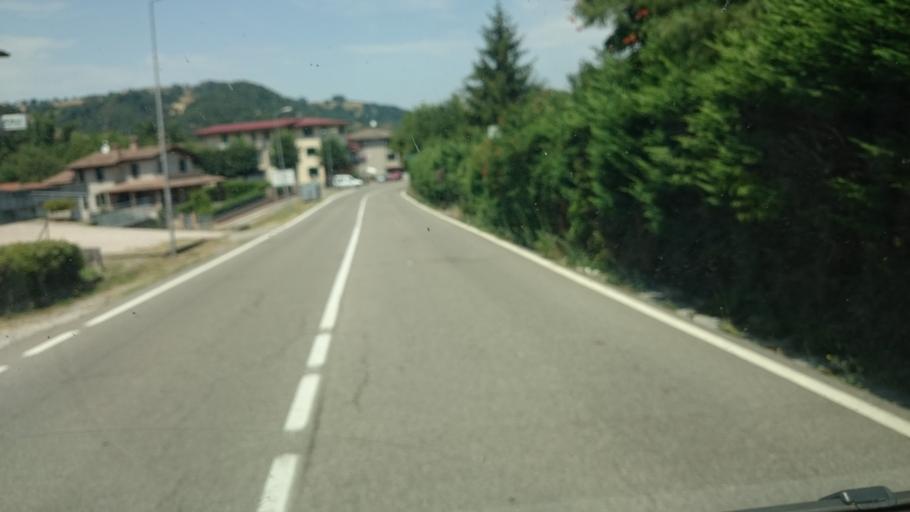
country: IT
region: Emilia-Romagna
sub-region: Provincia di Reggio Emilia
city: Vezzano sul Crostolo
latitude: 44.5597
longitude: 10.5291
